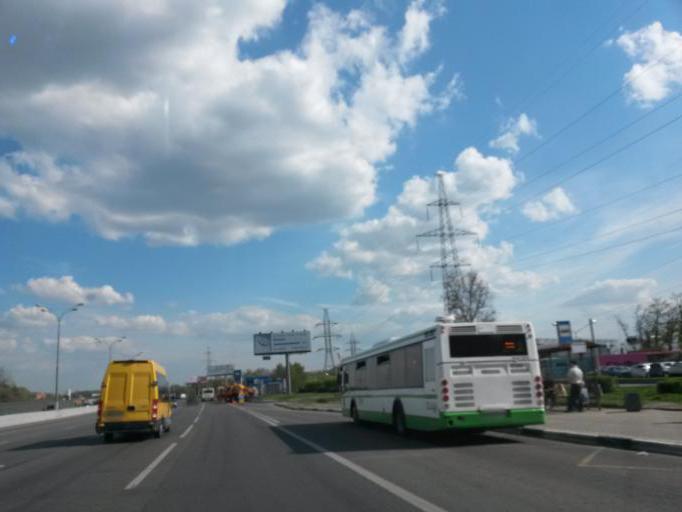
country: RU
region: Moscow
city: Yasenevo
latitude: 55.5993
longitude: 37.5056
